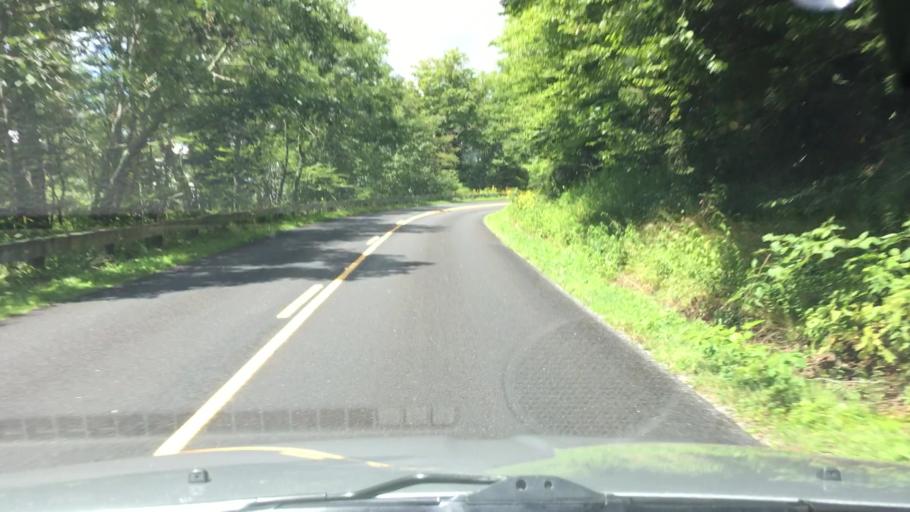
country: US
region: North Carolina
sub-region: Buncombe County
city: Black Mountain
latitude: 35.7470
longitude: -82.3394
